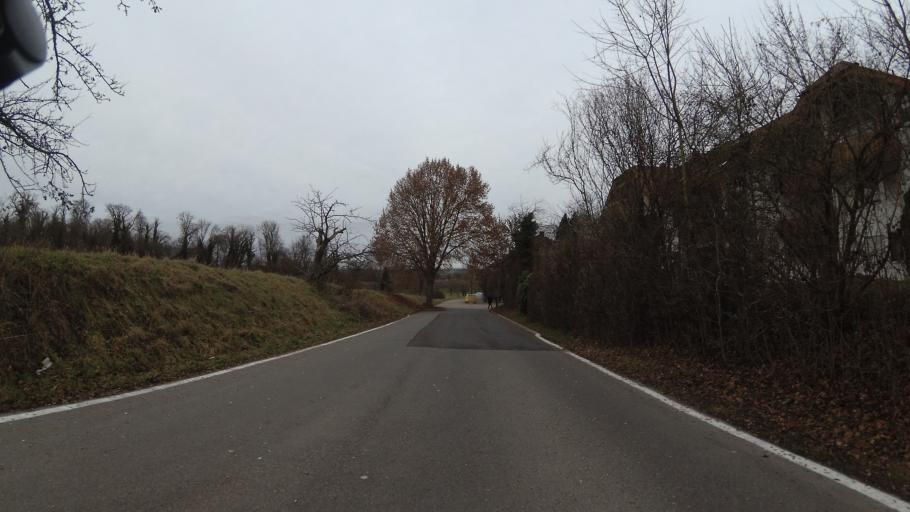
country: DE
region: Baden-Wuerttemberg
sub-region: Regierungsbezirk Stuttgart
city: Oedheim
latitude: 49.2335
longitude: 9.2487
